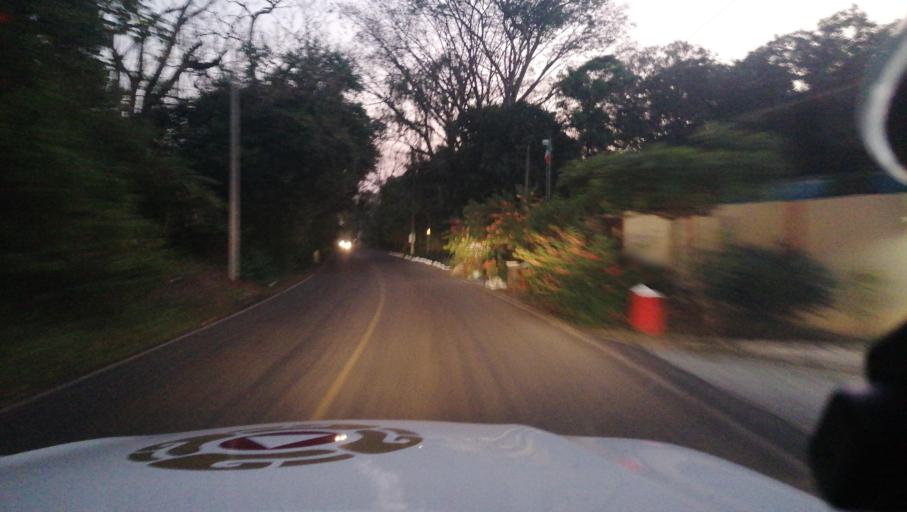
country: MX
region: Chiapas
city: Veinte de Noviembre
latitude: 14.9615
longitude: -92.2538
